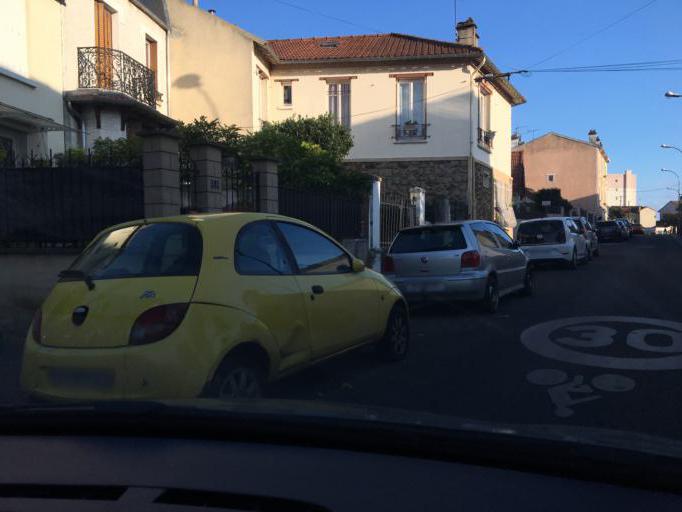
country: FR
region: Ile-de-France
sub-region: Departement du Val-de-Marne
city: Fontenay-sous-Bois
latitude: 48.8538
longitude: 2.4712
